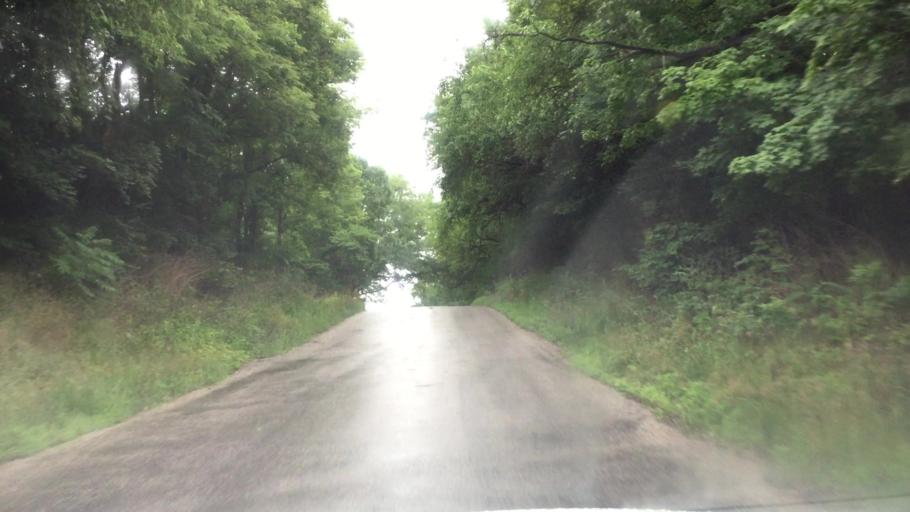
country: US
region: Iowa
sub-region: Lee County
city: Keokuk
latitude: 40.4263
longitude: -91.3656
